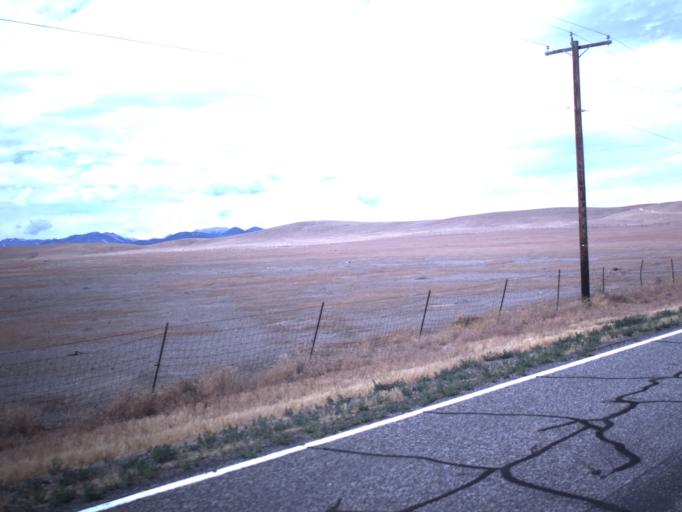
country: US
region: Utah
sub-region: Sevier County
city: Monroe
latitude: 38.6289
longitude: -112.1606
